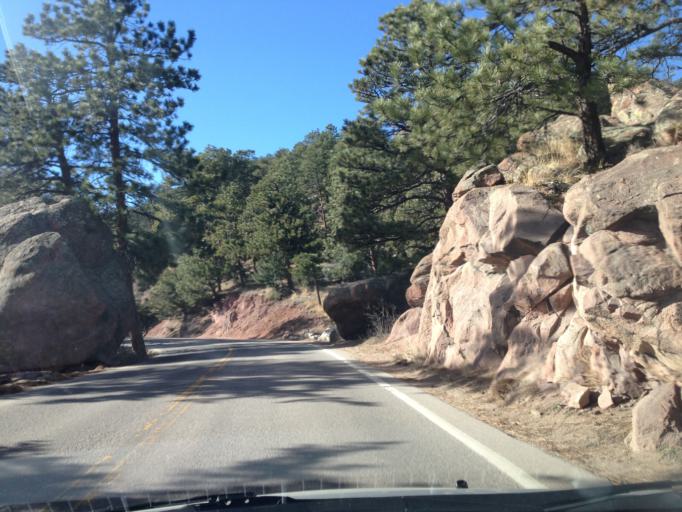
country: US
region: Colorado
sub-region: Boulder County
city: Boulder
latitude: 40.0029
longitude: -105.2953
